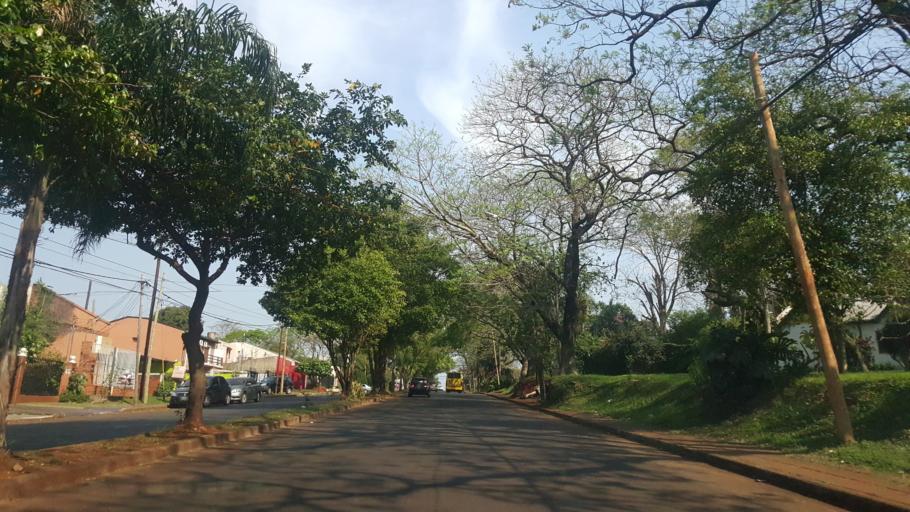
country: AR
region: Misiones
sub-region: Departamento de Capital
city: Posadas
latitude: -27.4005
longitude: -55.9073
